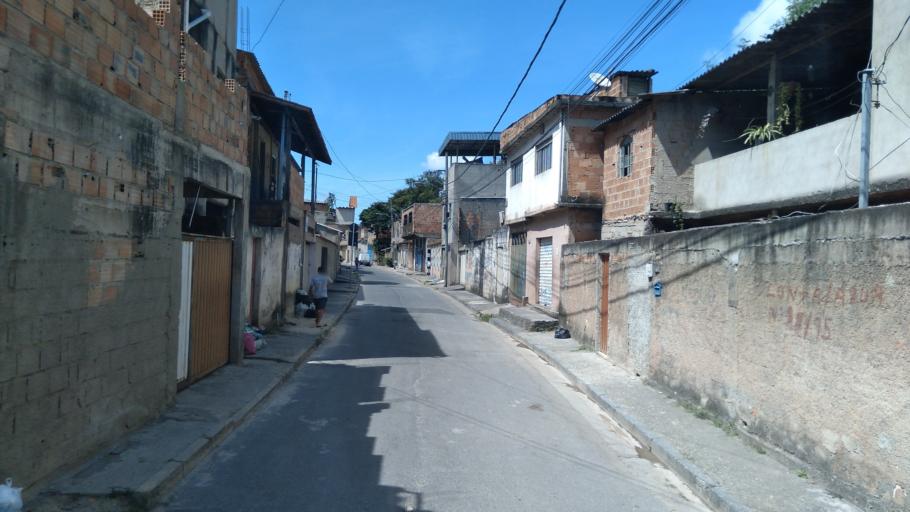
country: BR
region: Minas Gerais
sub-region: Belo Horizonte
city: Belo Horizonte
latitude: -19.8454
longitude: -43.8991
